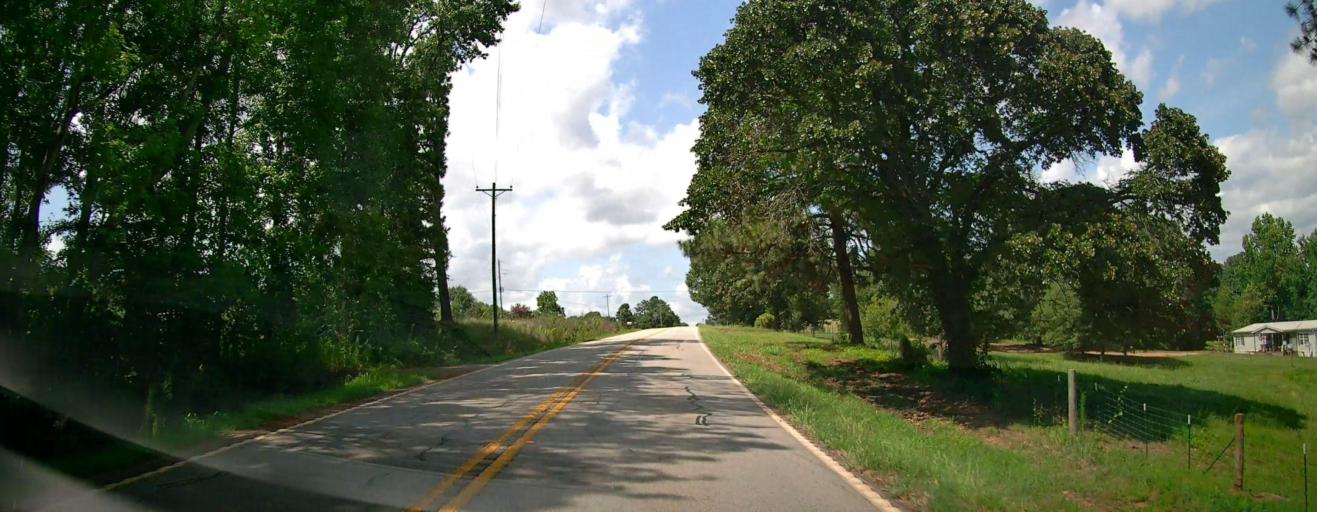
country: US
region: Georgia
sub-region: Carroll County
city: Bowdon
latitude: 33.4202
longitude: -85.2663
